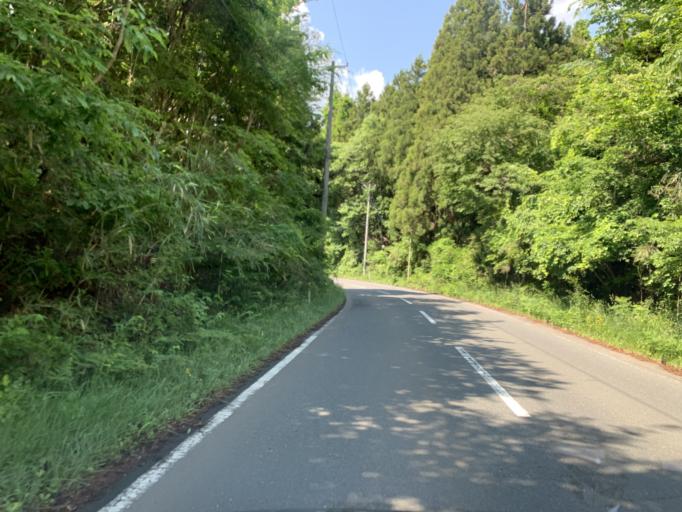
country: JP
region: Miyagi
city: Furukawa
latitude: 38.7130
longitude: 140.9426
